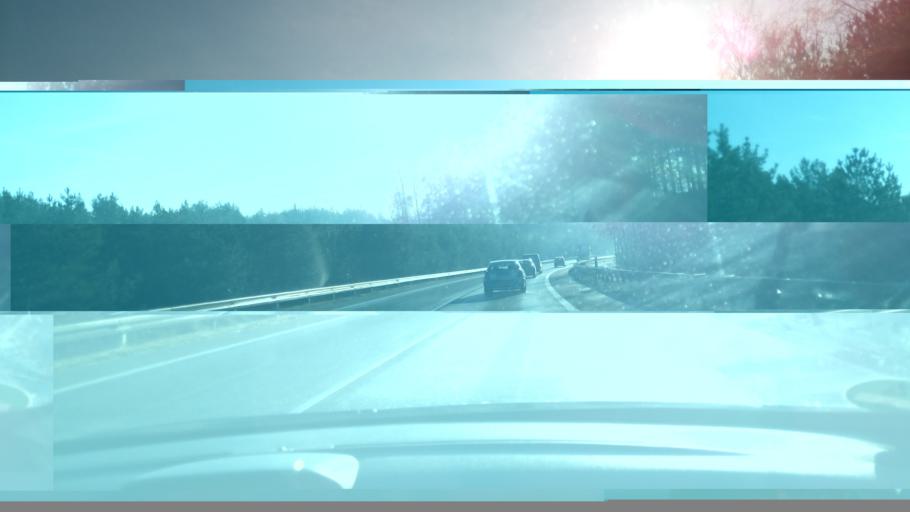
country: DE
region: Mecklenburg-Vorpommern
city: Neustrelitz
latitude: 53.3692
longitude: 13.0898
